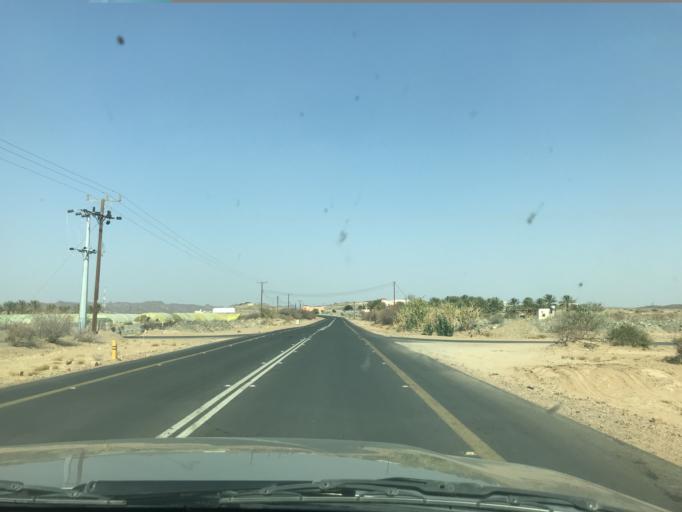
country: SA
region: Mintaqat al Bahah
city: Al Bahah
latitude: 20.4346
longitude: 41.9111
